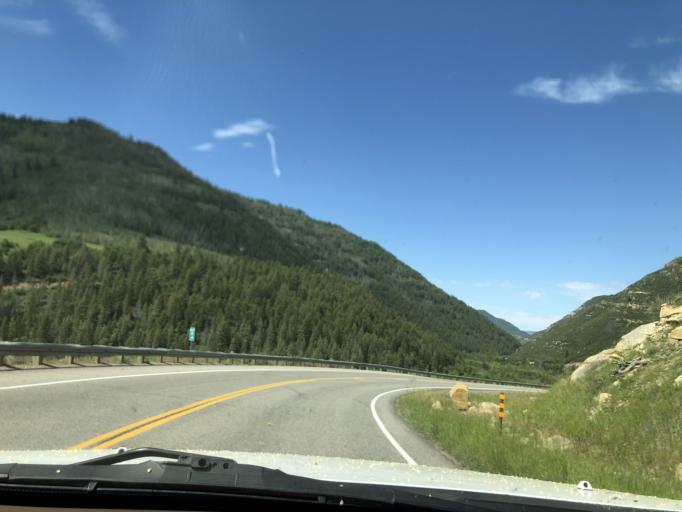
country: US
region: Colorado
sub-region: Delta County
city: Paonia
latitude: 38.9413
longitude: -107.3577
